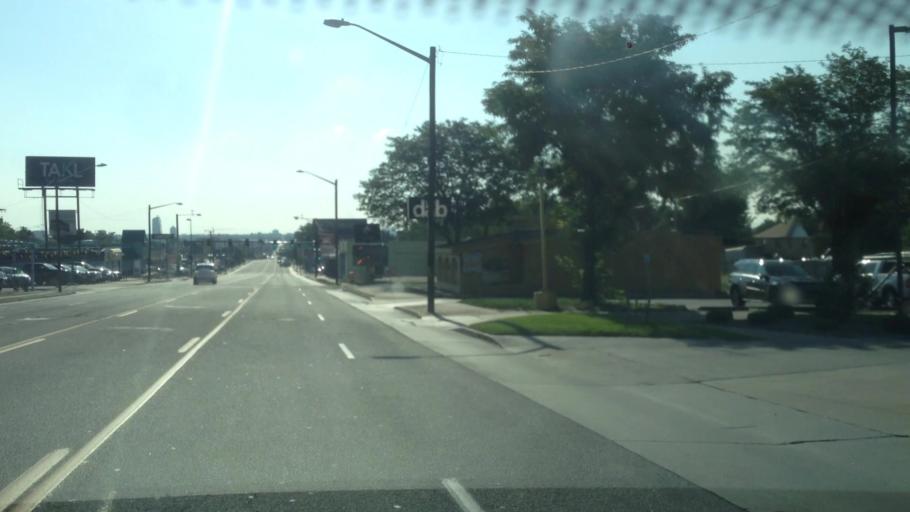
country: US
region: Colorado
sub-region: Denver County
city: Denver
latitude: 39.7111
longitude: -105.0225
